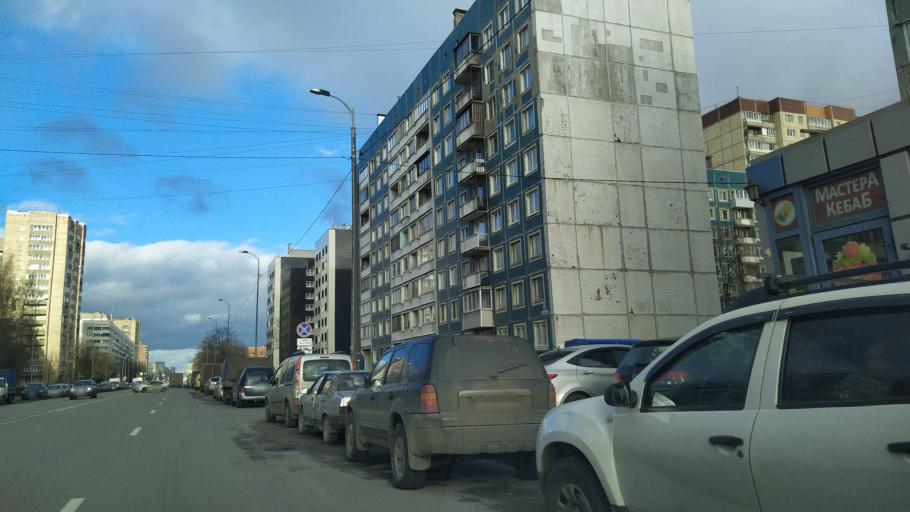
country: RU
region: Leningrad
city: Akademicheskoe
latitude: 60.0339
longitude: 30.3797
